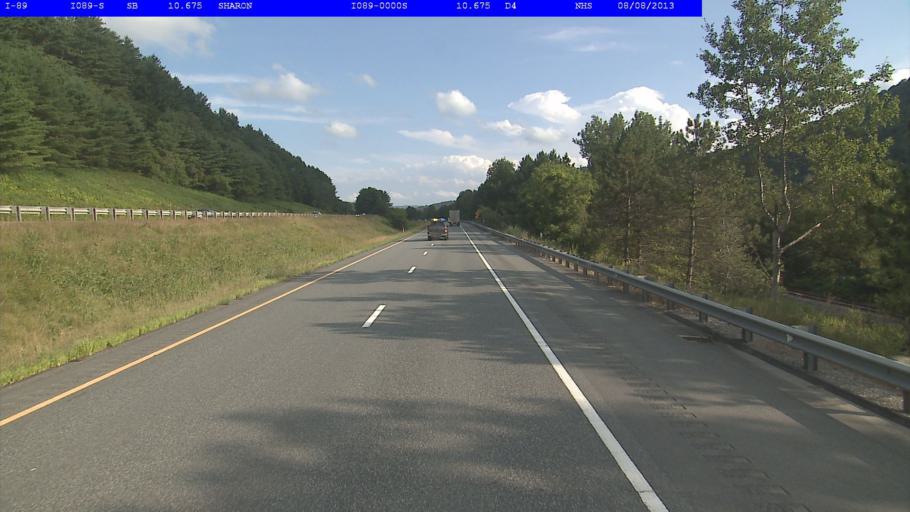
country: US
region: Vermont
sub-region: Windsor County
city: Woodstock
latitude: 43.7497
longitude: -72.4444
